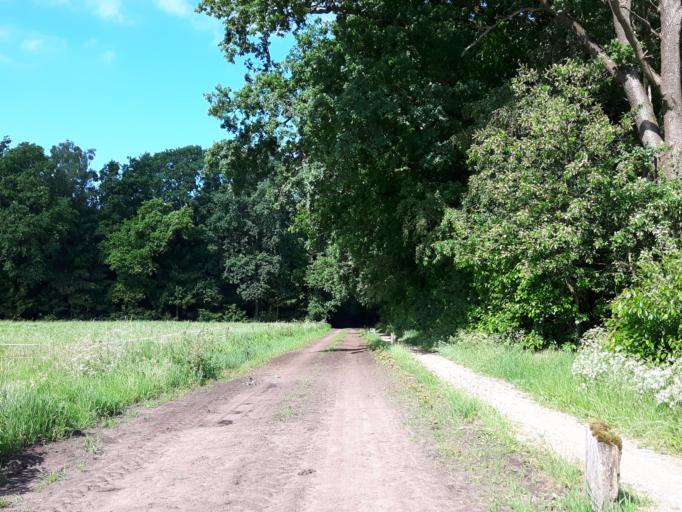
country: NL
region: Overijssel
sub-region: Gemeente Enschede
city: Enschede
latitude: 52.1699
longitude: 6.8279
